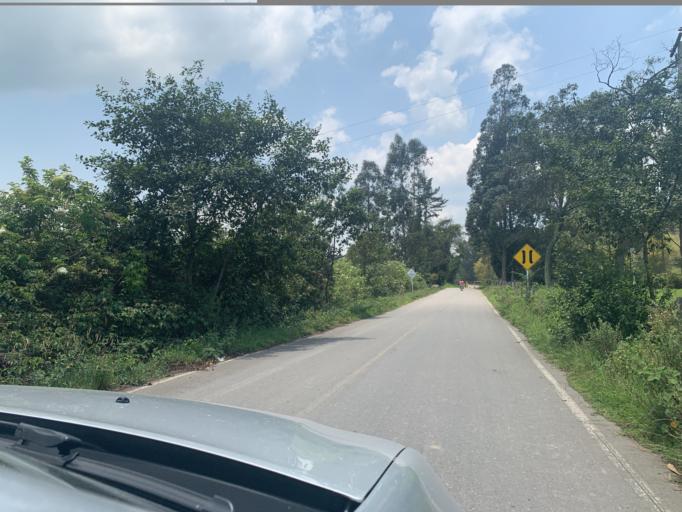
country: CO
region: Boyaca
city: Chiquinquira
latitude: 5.5381
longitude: -73.7466
